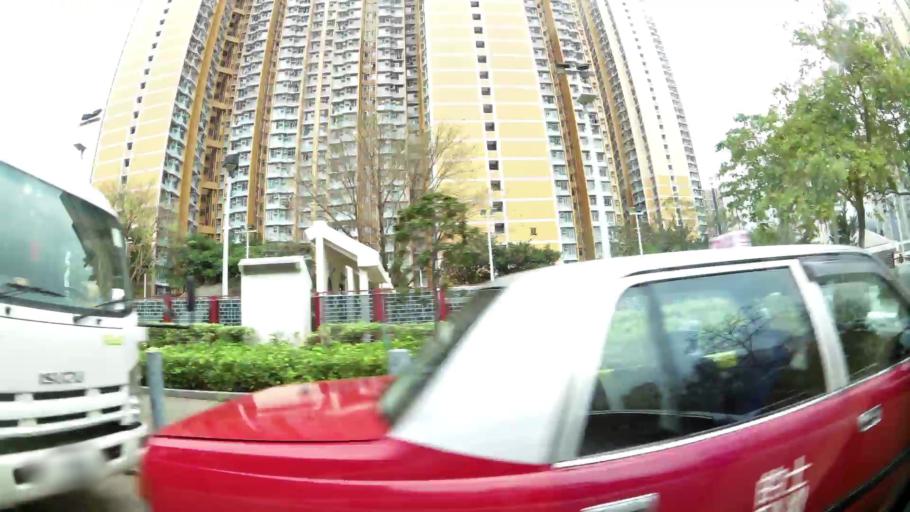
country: HK
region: Tsuen Wan
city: Tsuen Wan
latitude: 22.3669
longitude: 114.1311
